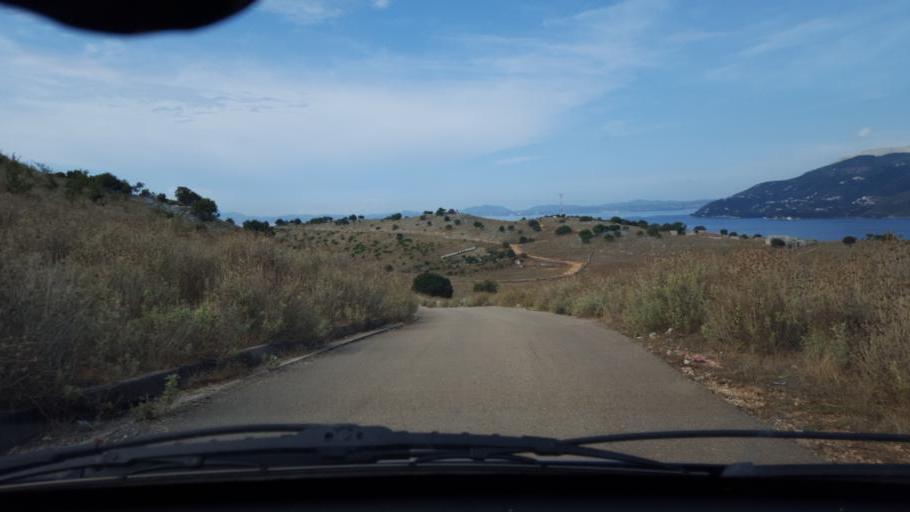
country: AL
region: Vlore
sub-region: Rrethi i Sarandes
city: Xarre
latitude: 39.7582
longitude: 19.9862
